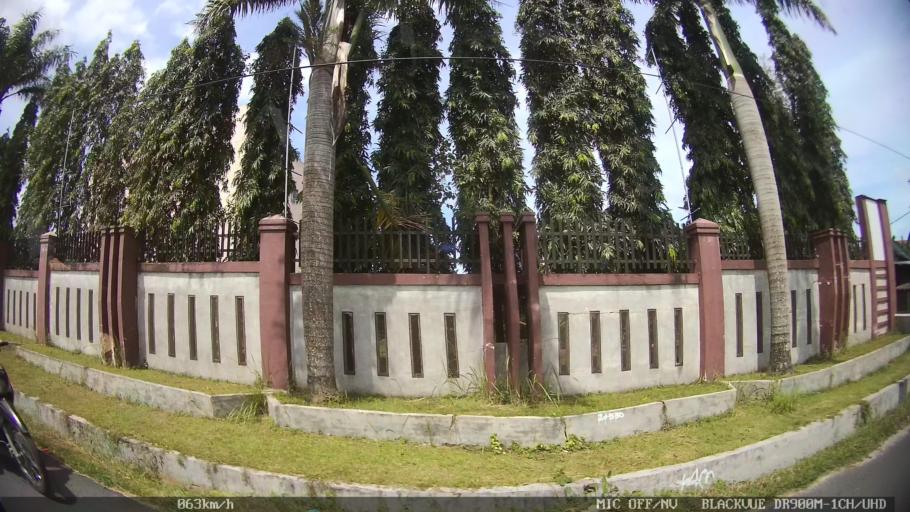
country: ID
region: North Sumatra
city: Percut
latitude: 3.5913
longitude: 98.8619
